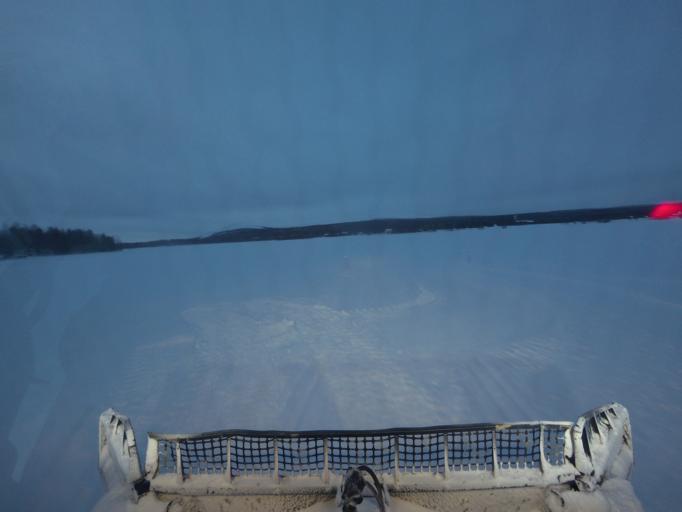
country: FI
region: Lapland
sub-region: Tunturi-Lappi
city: Kolari
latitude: 67.6124
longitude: 24.1476
